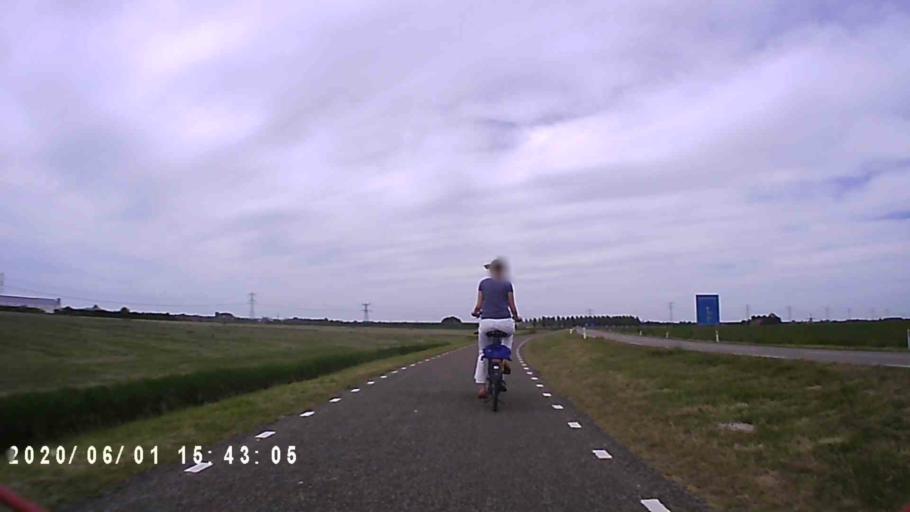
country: NL
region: Friesland
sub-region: Gemeente Boarnsterhim
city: Wergea
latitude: 53.1603
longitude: 5.8275
